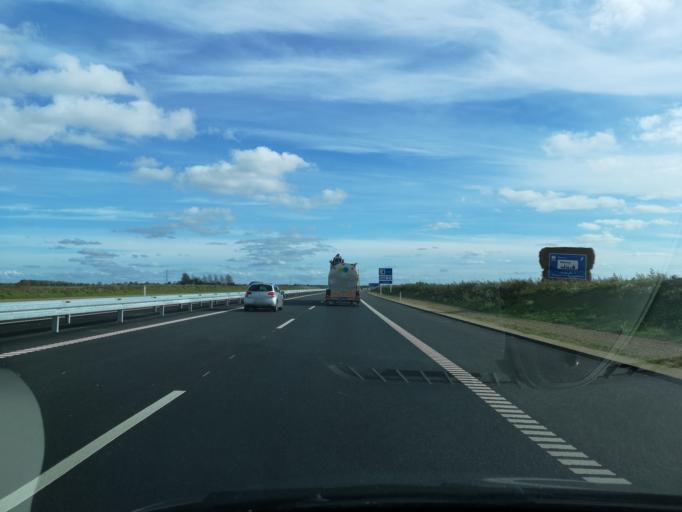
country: DK
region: Central Jutland
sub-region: Holstebro Kommune
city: Holstebro
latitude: 56.3738
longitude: 8.7073
